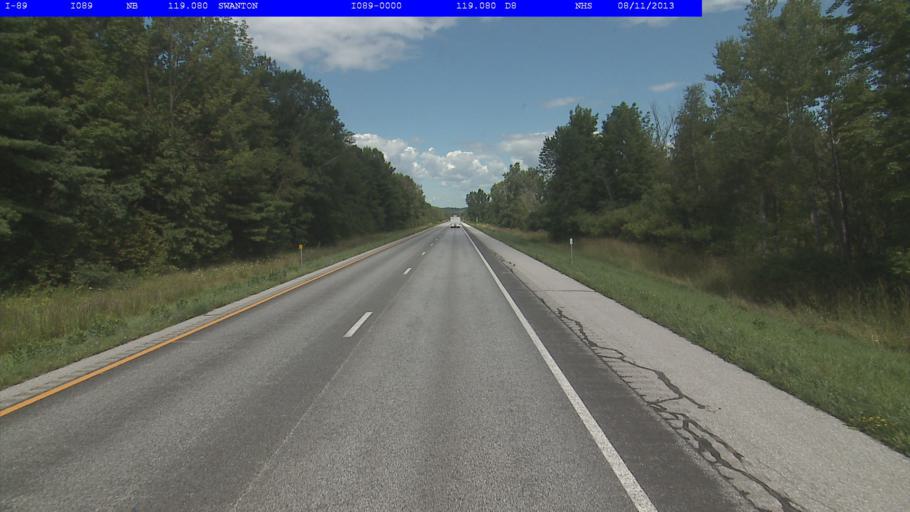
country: US
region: Vermont
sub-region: Franklin County
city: Saint Albans
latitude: 44.8640
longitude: -73.0809
